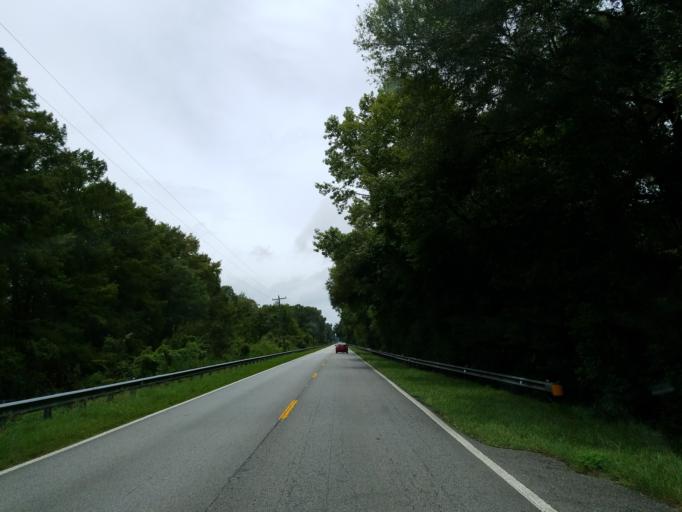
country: US
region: Florida
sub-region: Citrus County
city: Floral City
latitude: 28.7132
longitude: -82.2317
